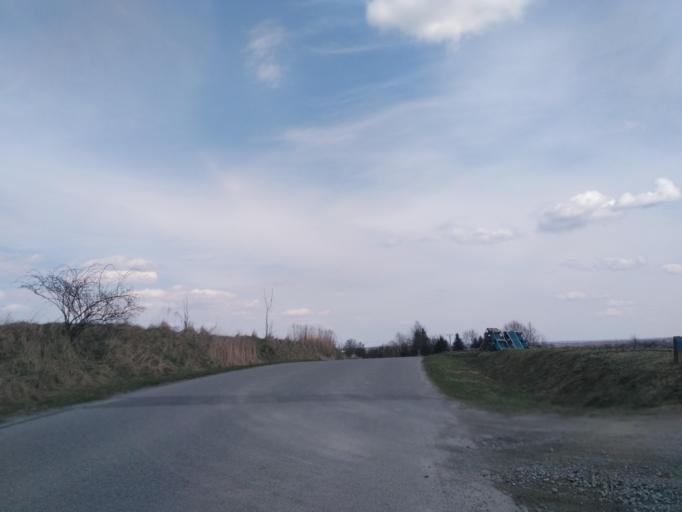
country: PL
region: Subcarpathian Voivodeship
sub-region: Powiat ropczycko-sedziszowski
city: Sedziszow Malopolski
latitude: 50.0444
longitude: 21.7102
